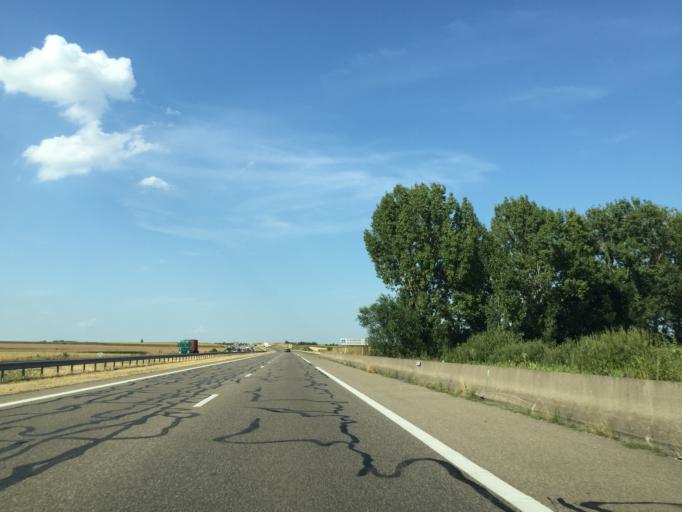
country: FR
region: Alsace
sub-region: Departement du Bas-Rhin
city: Krautergersheim
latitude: 48.4852
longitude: 7.5520
